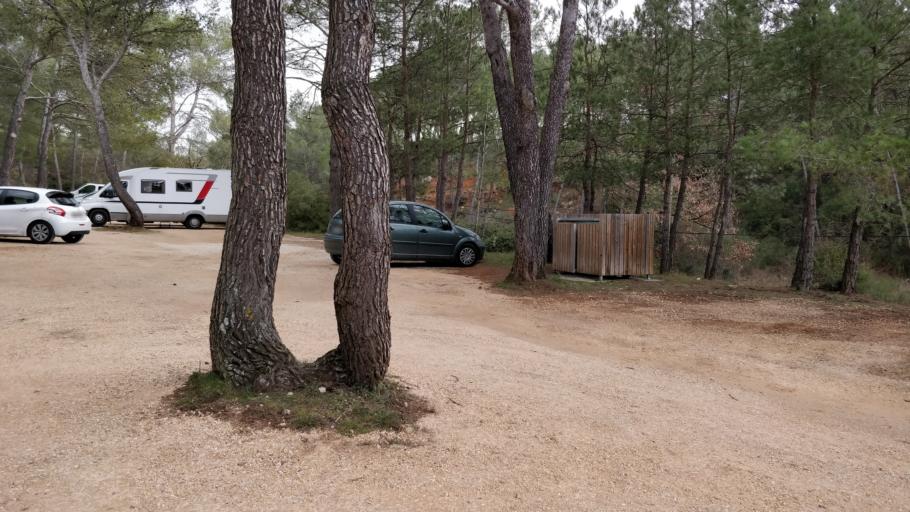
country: FR
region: Provence-Alpes-Cote d'Azur
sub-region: Departement des Bouches-du-Rhone
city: Le Tholonet
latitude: 43.5214
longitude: 5.5271
